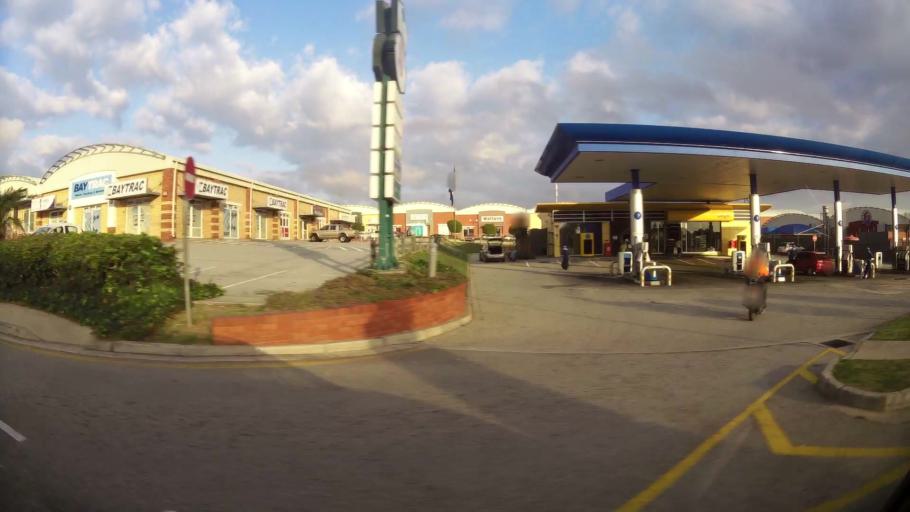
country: ZA
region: Eastern Cape
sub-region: Nelson Mandela Bay Metropolitan Municipality
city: Port Elizabeth
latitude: -33.9805
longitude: 25.5531
